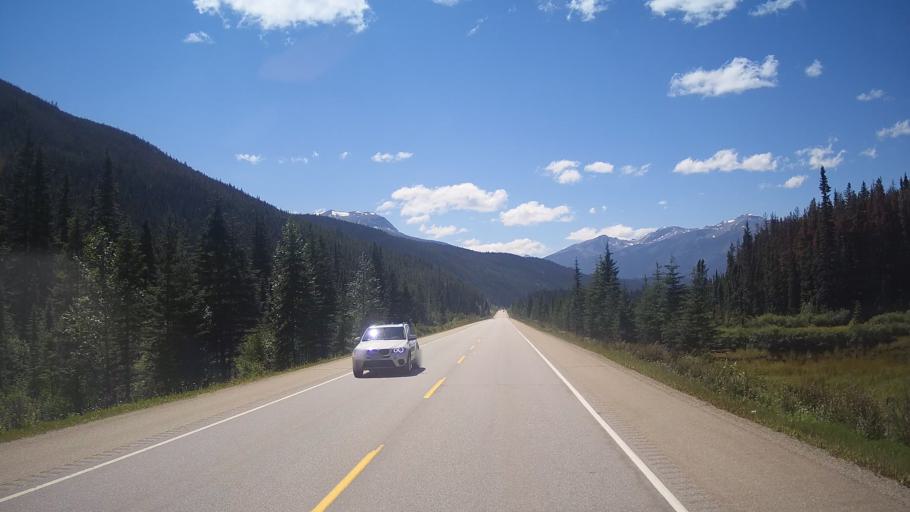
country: CA
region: Alberta
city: Jasper Park Lodge
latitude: 52.8836
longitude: -118.4863
